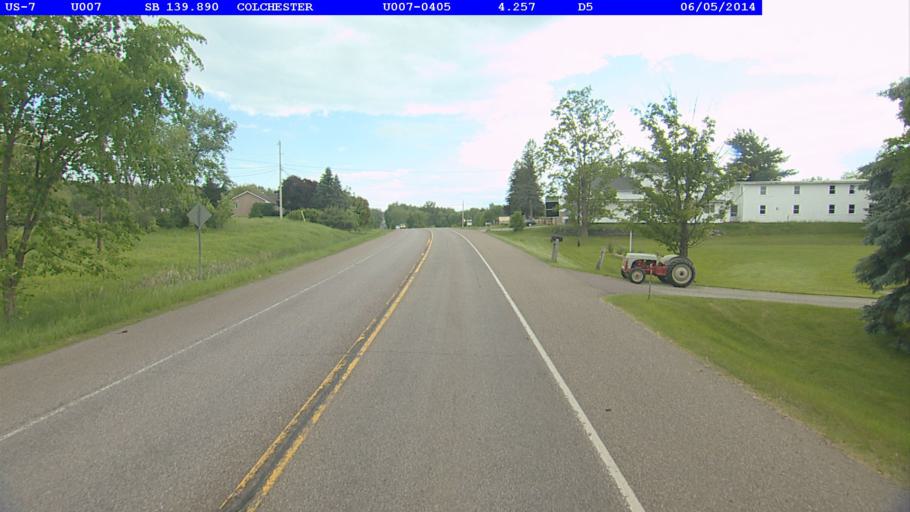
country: US
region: Vermont
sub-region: Chittenden County
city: Colchester
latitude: 44.5599
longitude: -73.1613
